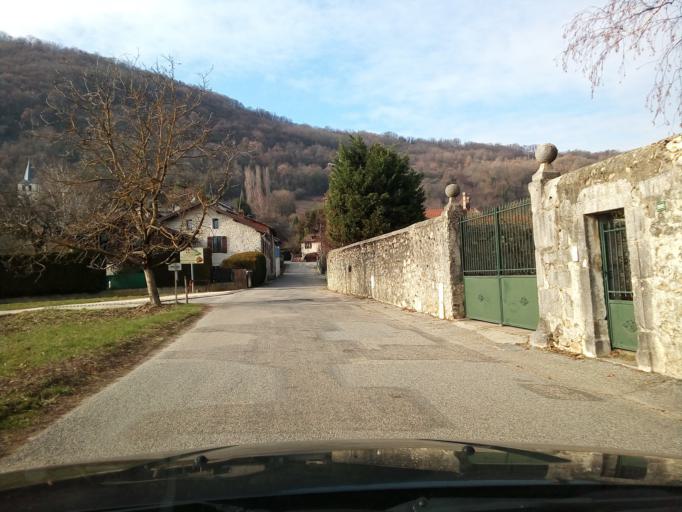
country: FR
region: Rhone-Alpes
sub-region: Departement de l'Isere
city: Chapareillan
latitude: 45.4716
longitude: 5.9829
